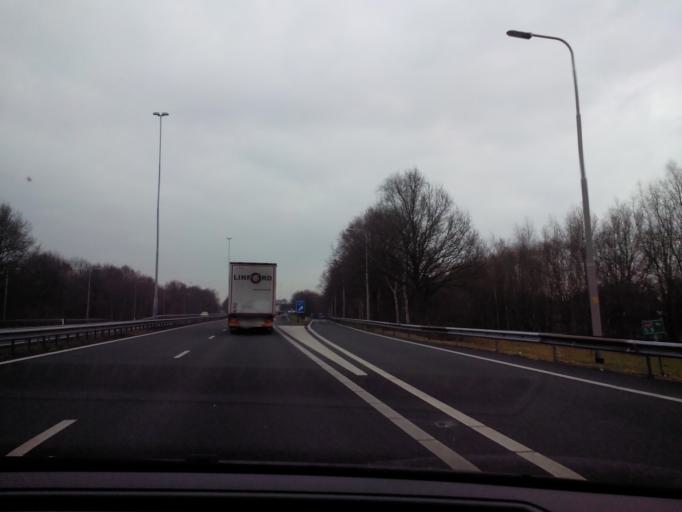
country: NL
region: North Brabant
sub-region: Gemeente Breda
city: Hoge Vucht
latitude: 51.5890
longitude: 4.8265
